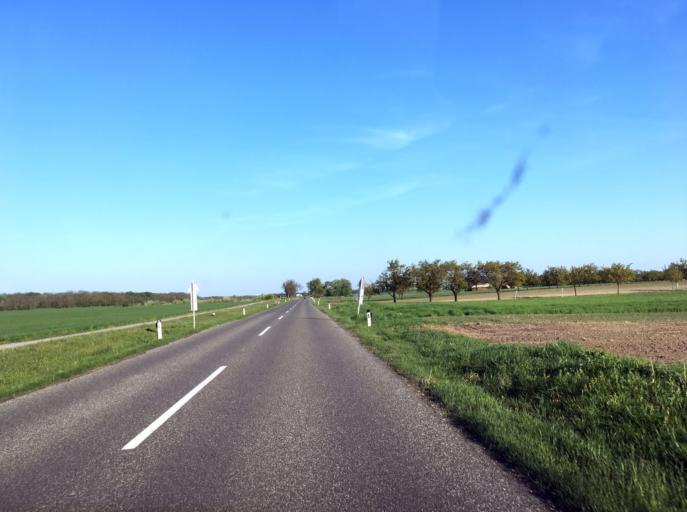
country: AT
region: Burgenland
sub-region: Politischer Bezirk Neusiedl am See
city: Kittsee
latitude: 48.0802
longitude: 17.0737
